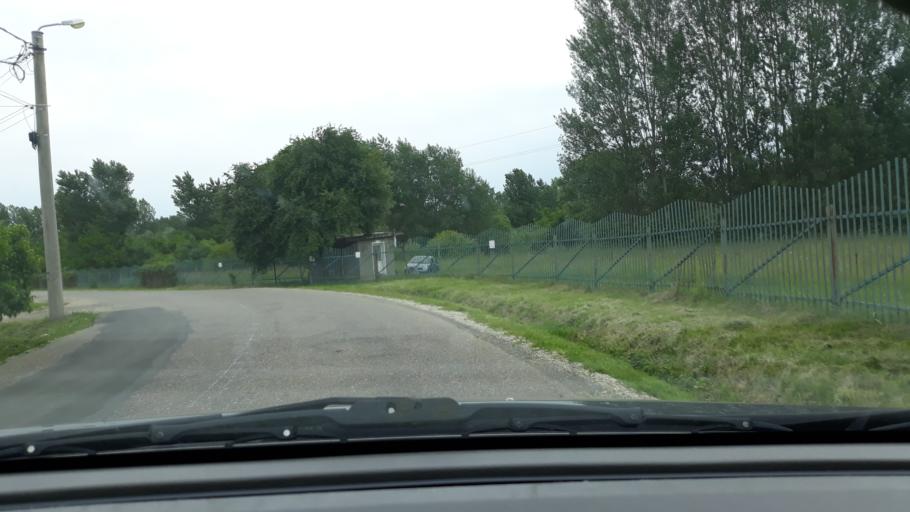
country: RO
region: Bihor
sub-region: Comuna Sanmartin
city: Sanmartin
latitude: 47.0527
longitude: 21.9987
